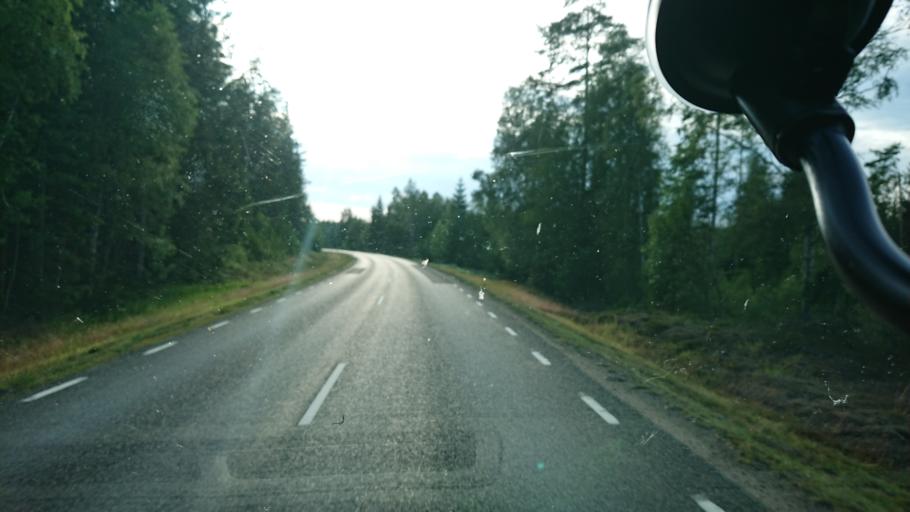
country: SE
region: Kronoberg
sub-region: Vaxjo Kommun
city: Braas
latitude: 57.0246
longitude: 15.0025
